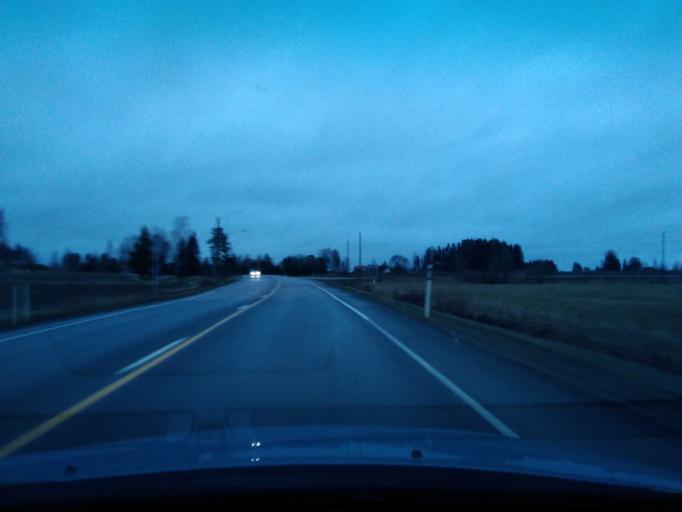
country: FI
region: Uusimaa
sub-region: Porvoo
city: Askola
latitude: 60.4447
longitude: 25.5851
